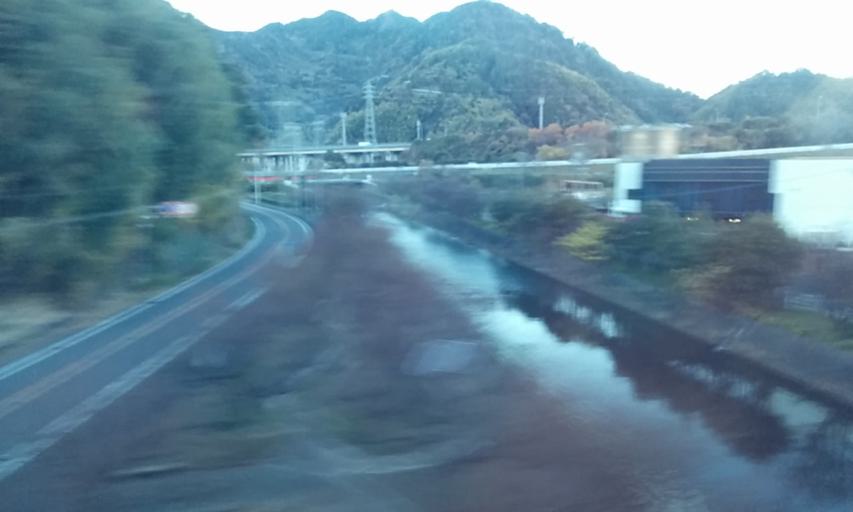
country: JP
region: Shizuoka
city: Shizuoka-shi
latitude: 34.9258
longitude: 138.3612
